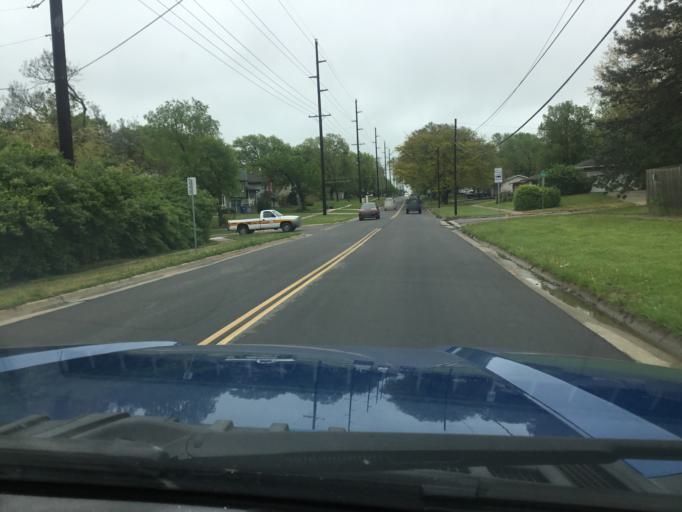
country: US
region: Kansas
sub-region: Shawnee County
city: Topeka
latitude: 39.0364
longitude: -95.7540
